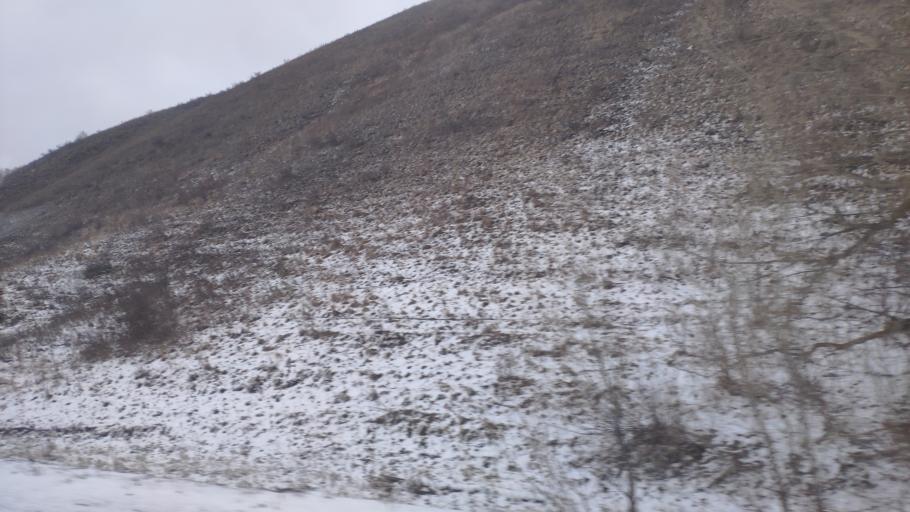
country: RU
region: Bashkortostan
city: Isyangulovo
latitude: 52.1615
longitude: 56.9152
